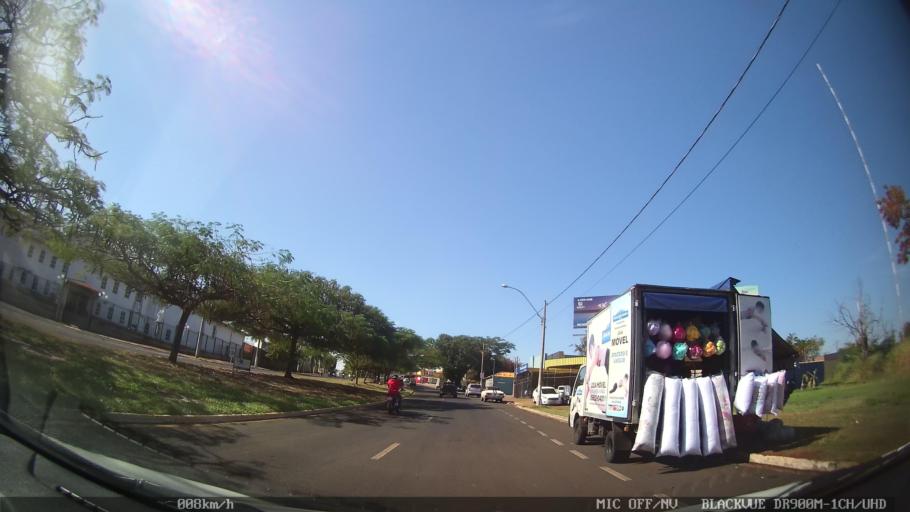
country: BR
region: Sao Paulo
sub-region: Ribeirao Preto
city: Ribeirao Preto
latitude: -21.2120
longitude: -47.7741
